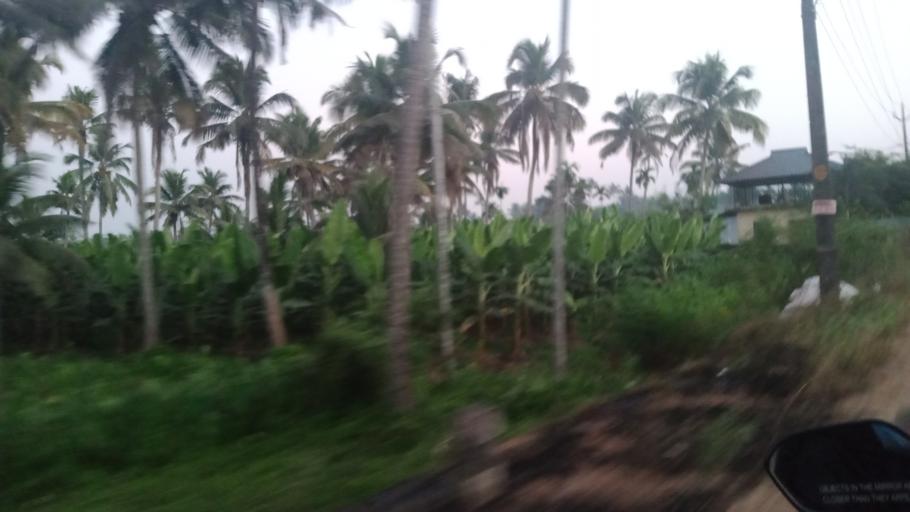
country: IN
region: Kerala
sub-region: Ernakulam
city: Angamali
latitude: 10.1988
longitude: 76.3075
